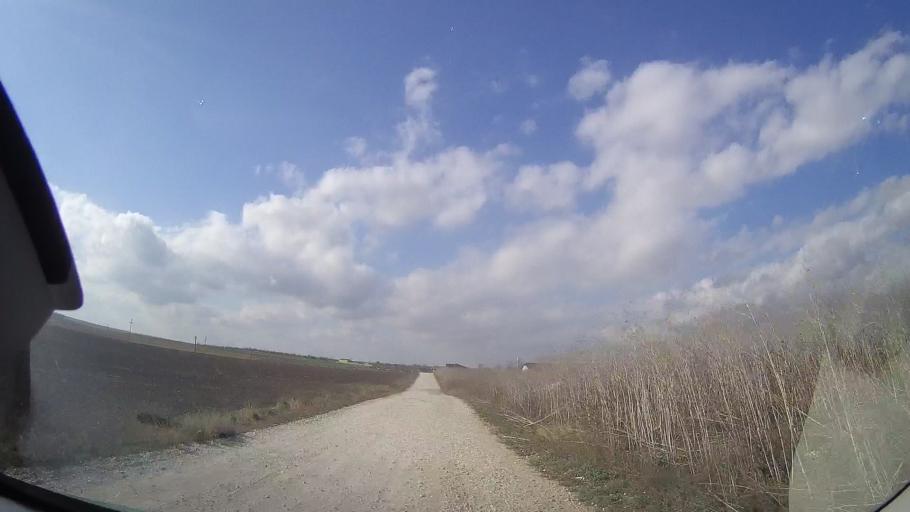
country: RO
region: Constanta
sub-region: Comuna Douazeci si Trei August
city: Douazeci si Trei August
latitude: 43.9116
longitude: 28.5930
